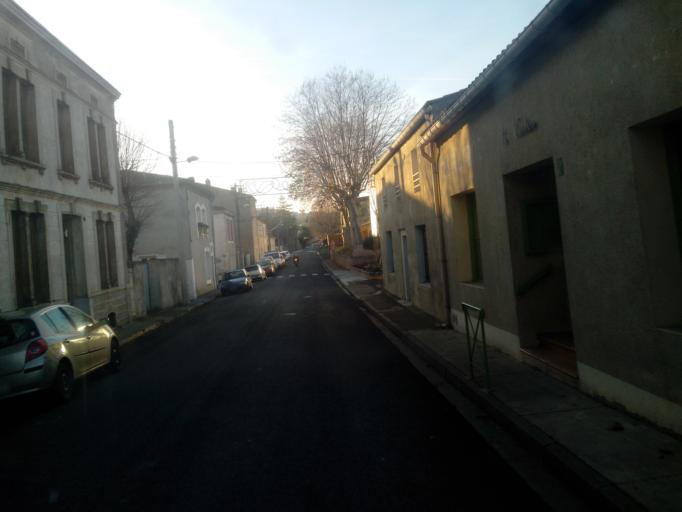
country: FR
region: Languedoc-Roussillon
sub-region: Departement de l'Aude
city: Esperaza
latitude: 42.9353
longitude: 2.2183
